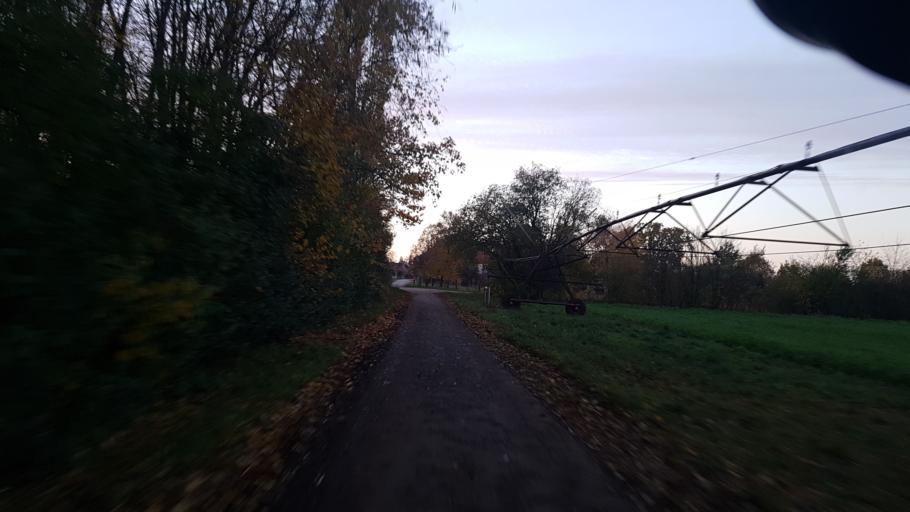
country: DE
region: Brandenburg
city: Bad Liebenwerda
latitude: 51.5141
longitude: 13.3061
